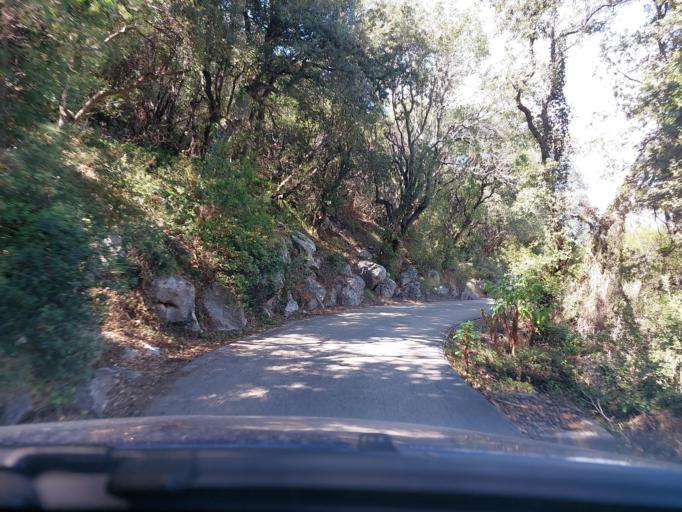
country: HR
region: Dubrovacko-Neretvanska
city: Smokvica
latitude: 42.7693
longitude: 16.8960
